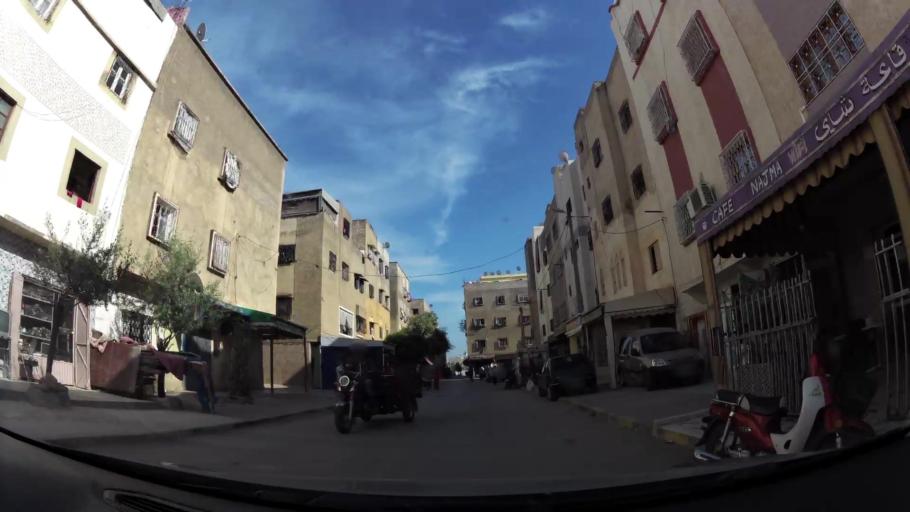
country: MA
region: Fes-Boulemane
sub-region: Fes
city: Fes
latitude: 34.0164
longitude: -5.0327
